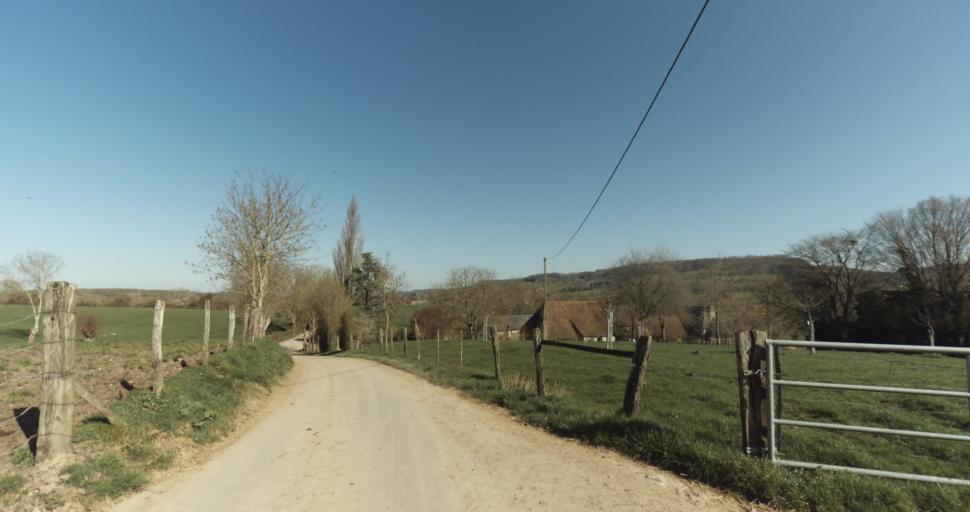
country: FR
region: Lower Normandy
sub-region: Departement du Calvados
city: Saint-Pierre-sur-Dives
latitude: 48.9677
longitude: 0.0390
